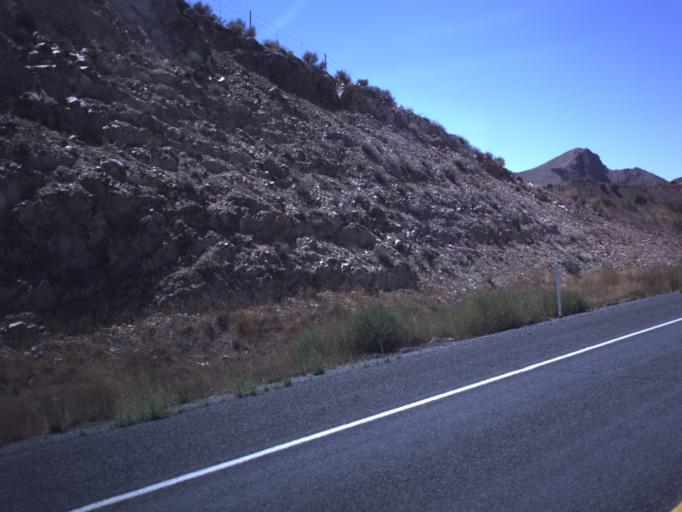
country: US
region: Utah
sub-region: Juab County
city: Nephi
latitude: 39.5786
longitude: -112.1769
